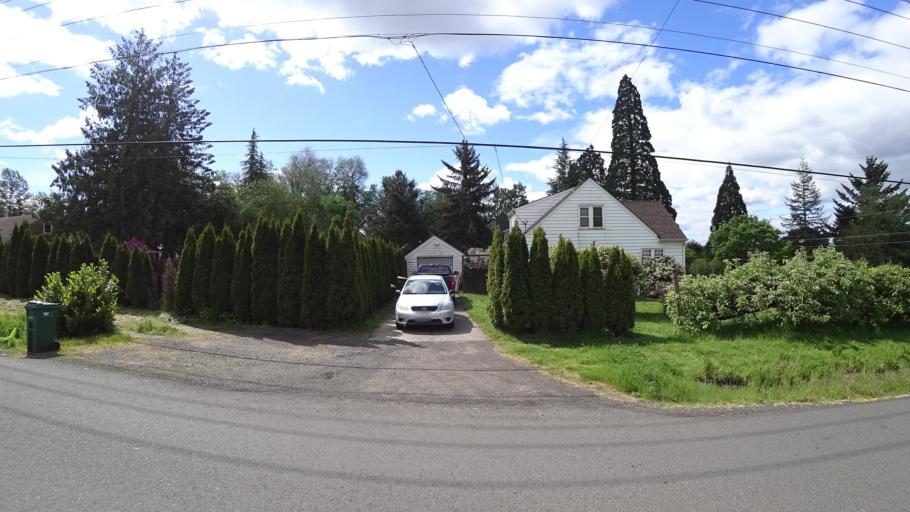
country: US
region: Oregon
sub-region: Washington County
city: Metzger
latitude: 45.4432
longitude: -122.7494
